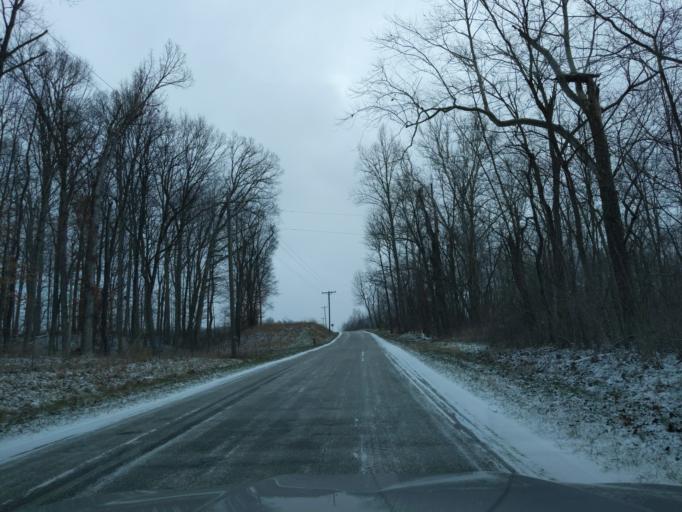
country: US
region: Indiana
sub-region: Decatur County
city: Greensburg
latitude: 39.2453
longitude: -85.4686
